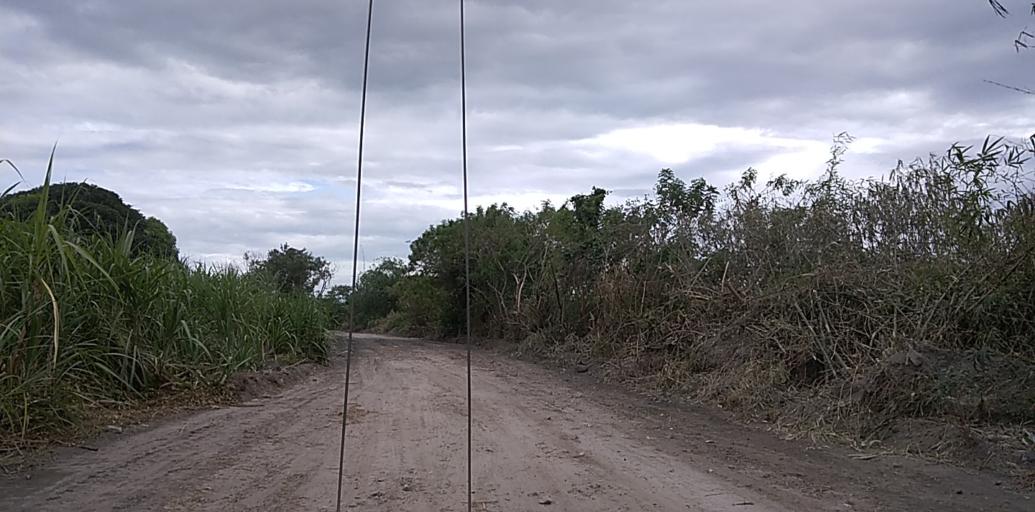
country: PH
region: Central Luzon
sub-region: Province of Pampanga
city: Pulung Santol
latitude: 15.0413
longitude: 120.5573
